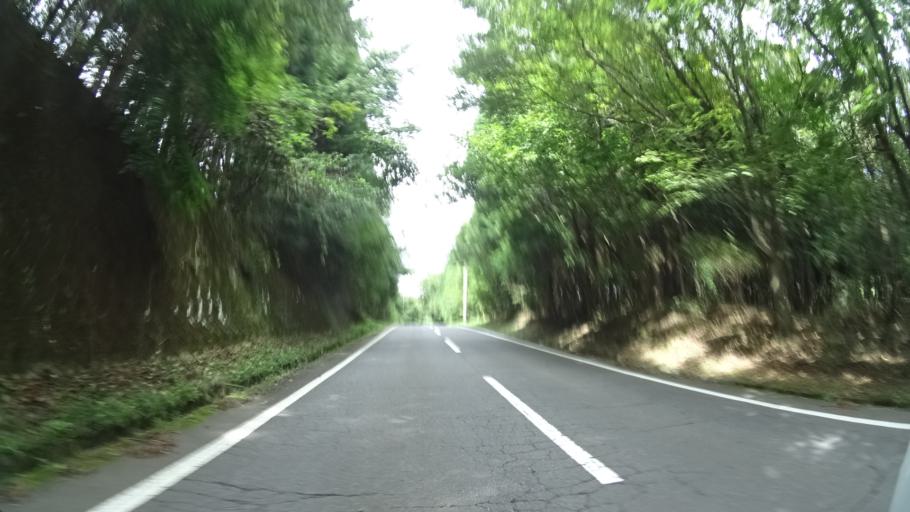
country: JP
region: Oita
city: Beppu
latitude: 33.3017
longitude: 131.3894
